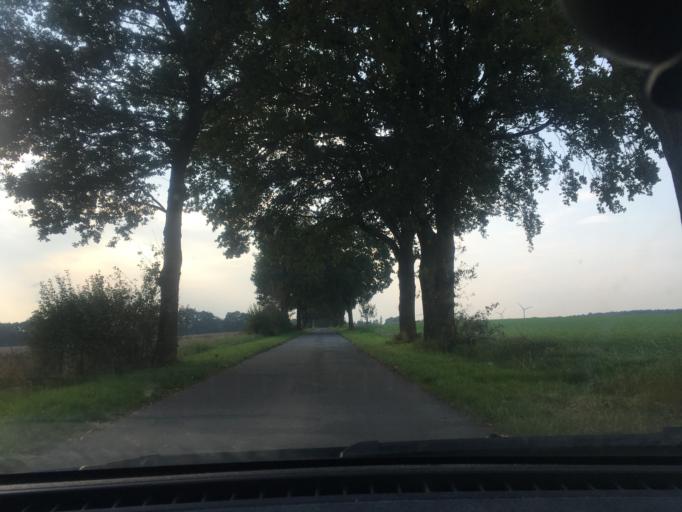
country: DE
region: Lower Saxony
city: Vastorf
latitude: 53.2049
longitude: 10.5556
